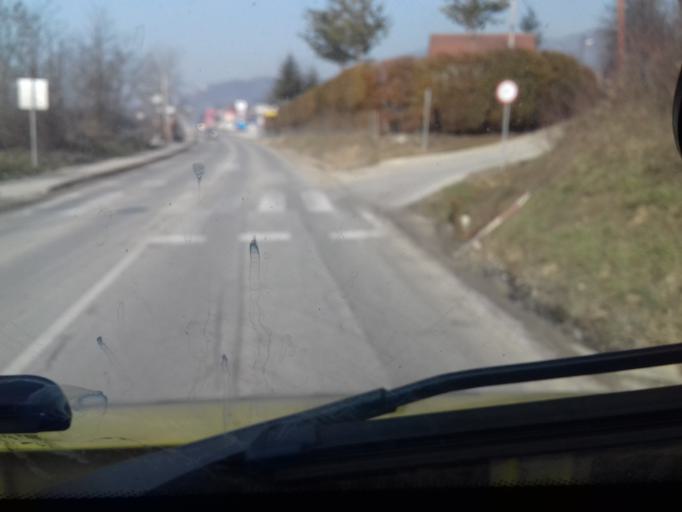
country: BA
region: Federation of Bosnia and Herzegovina
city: Vogosca
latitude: 43.9129
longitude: 18.3227
